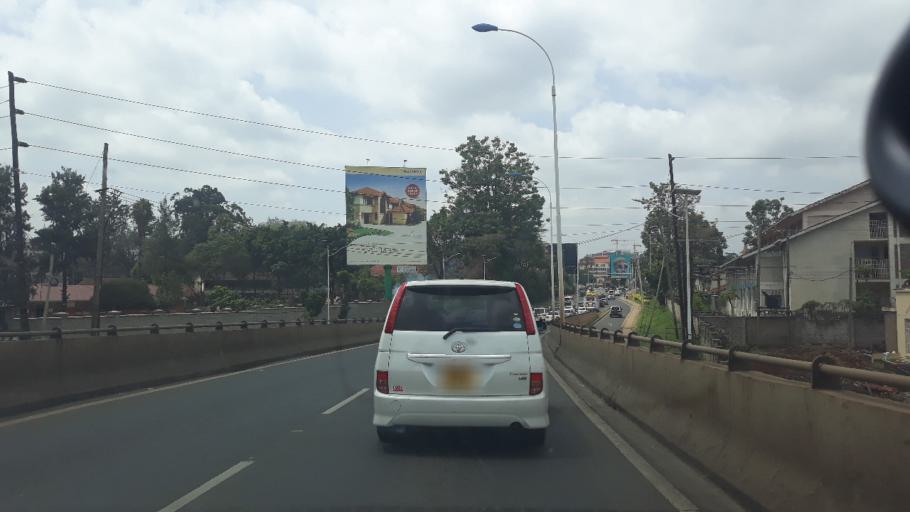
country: KE
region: Nairobi Area
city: Nairobi
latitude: -1.2691
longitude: 36.8198
